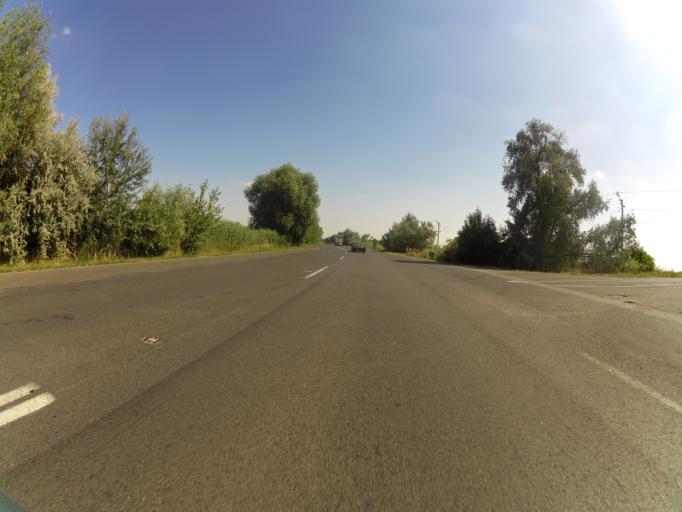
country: HU
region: Csongrad
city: Szatymaz
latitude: 46.3134
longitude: 20.0650
